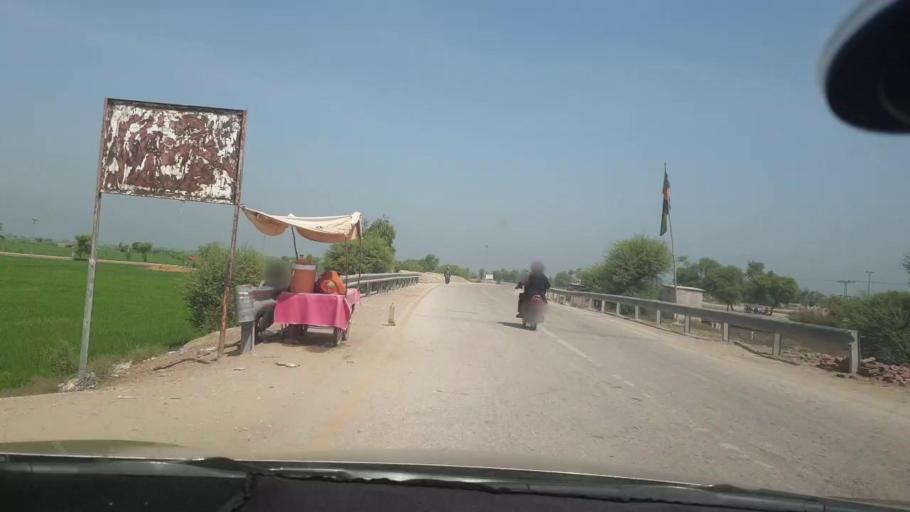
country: PK
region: Sindh
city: Shahdadkot
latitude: 27.7273
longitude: 67.9618
